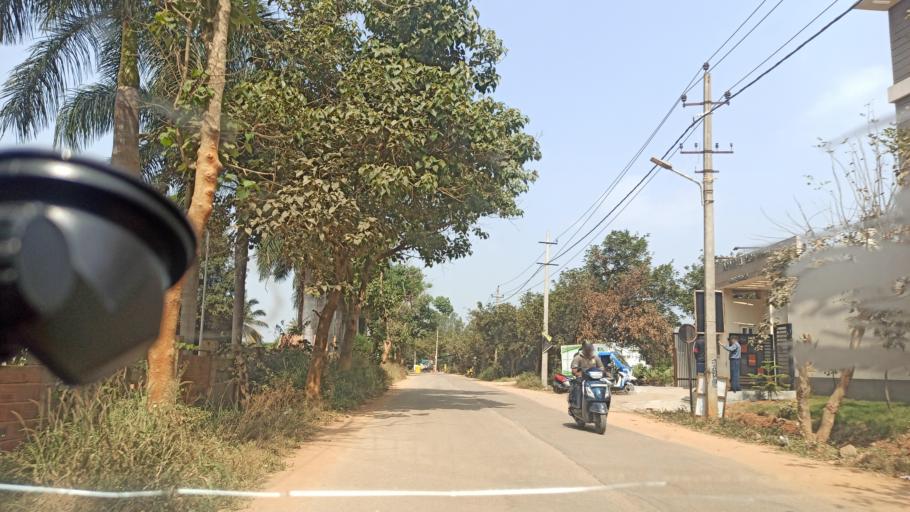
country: IN
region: Karnataka
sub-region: Bangalore Urban
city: Yelahanka
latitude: 13.0962
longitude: 77.6185
